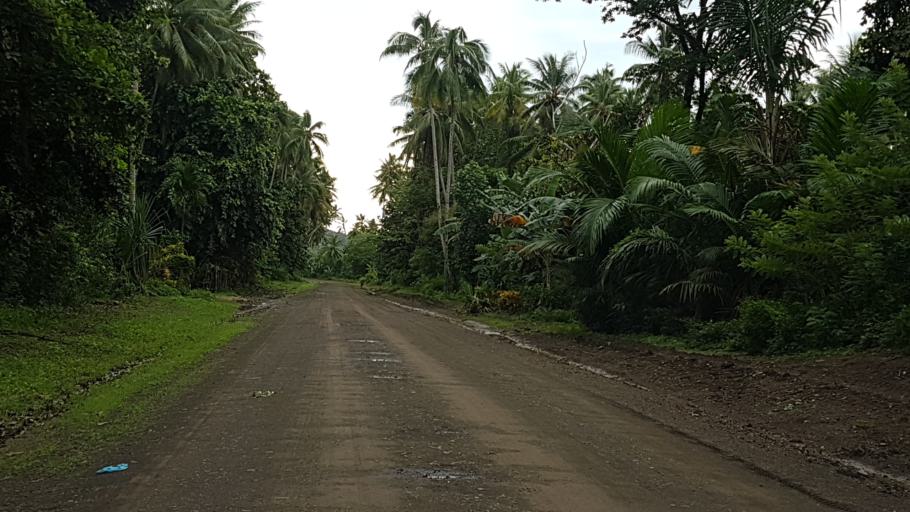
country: PG
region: Milne Bay
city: Alotau
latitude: -10.3236
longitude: 150.6917
